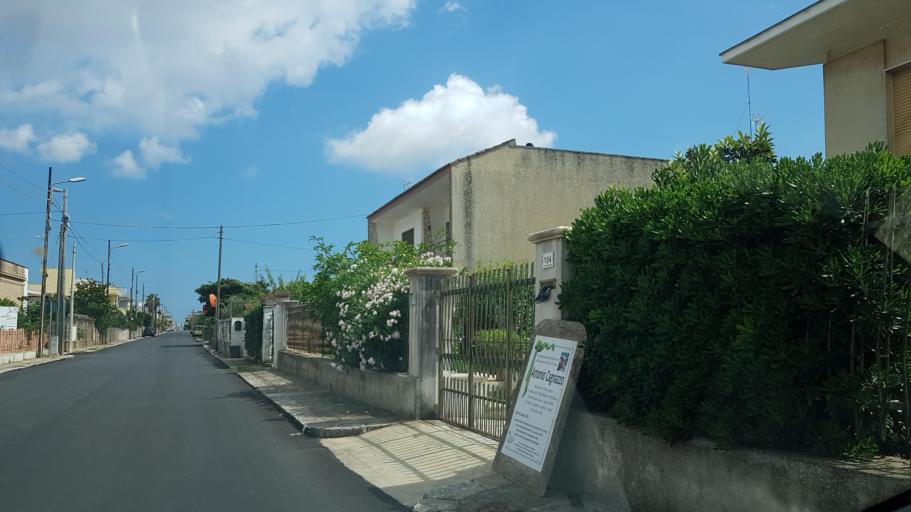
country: IT
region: Apulia
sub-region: Provincia di Lecce
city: Patu
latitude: 39.8408
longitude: 18.3414
